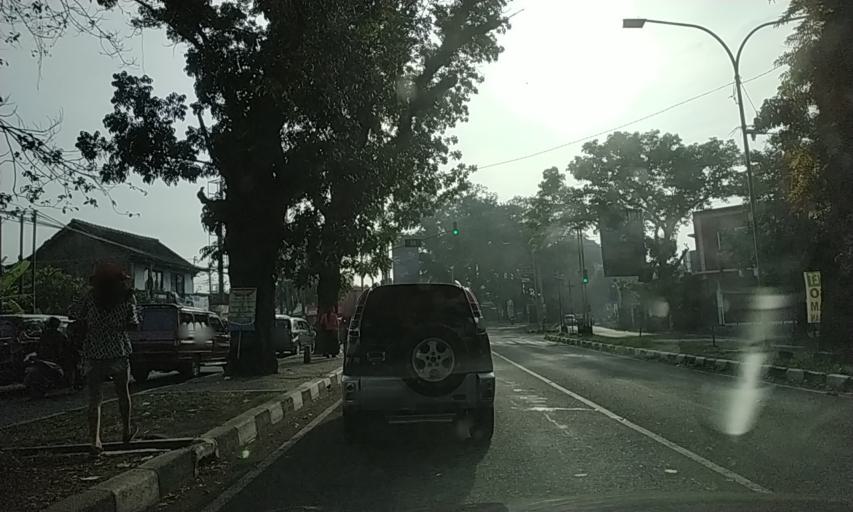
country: ID
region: Central Java
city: Candi Prambanan
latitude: -7.7576
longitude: 110.4799
